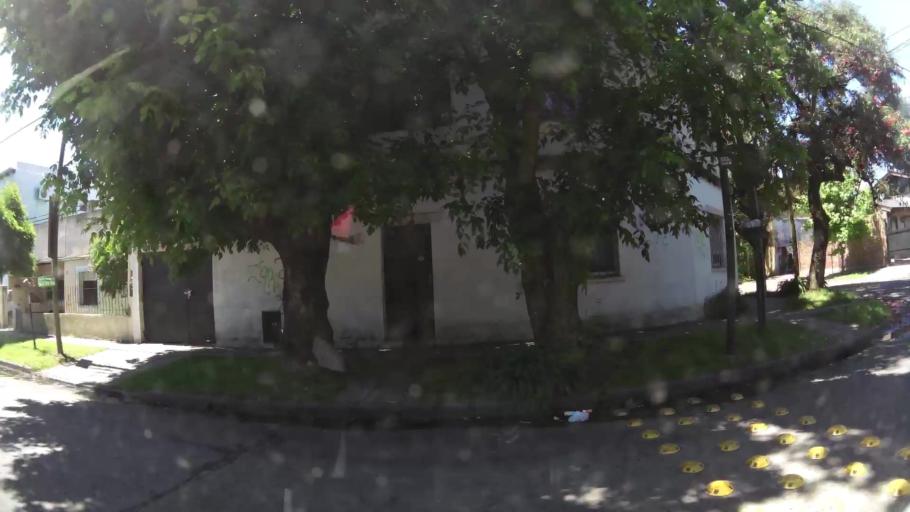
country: AR
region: Buenos Aires
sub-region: Partido de San Isidro
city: San Isidro
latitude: -34.5062
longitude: -58.5691
